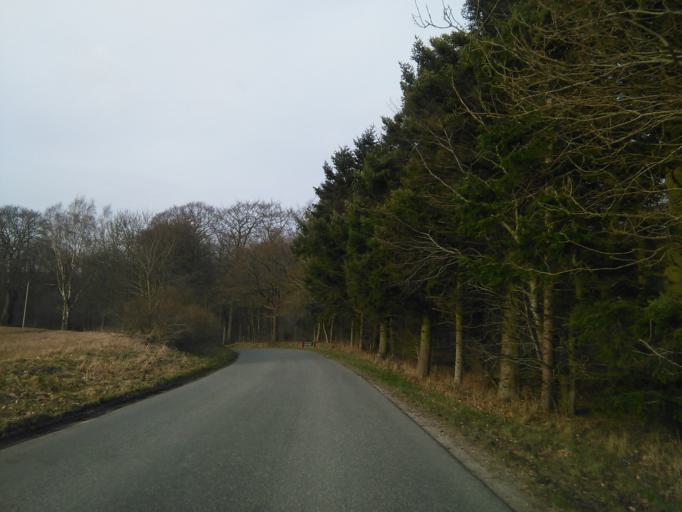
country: DK
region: Central Jutland
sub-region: Arhus Kommune
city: Beder
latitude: 56.0649
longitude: 10.2436
